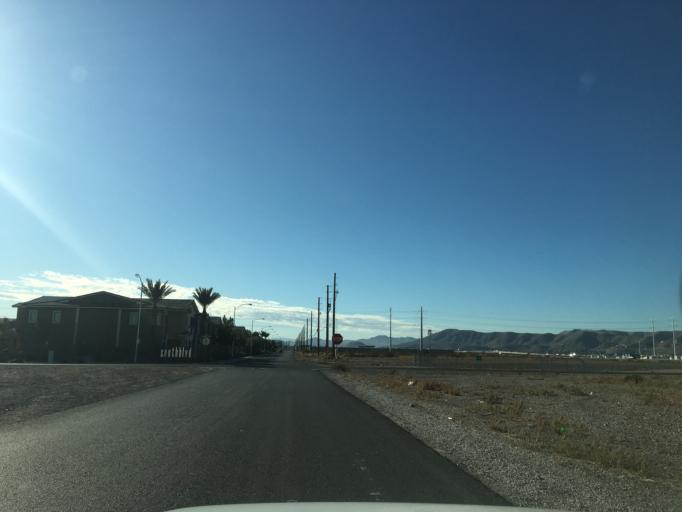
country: US
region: Nevada
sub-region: Clark County
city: Enterprise
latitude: 36.0070
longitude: -115.1703
